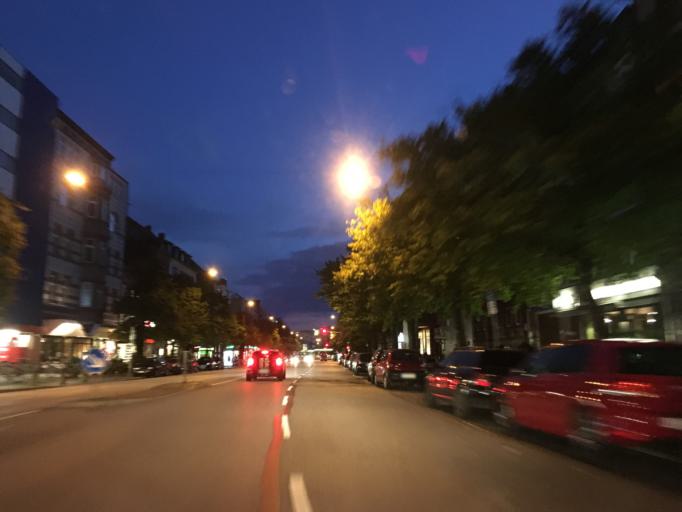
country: DE
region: Schleswig-Holstein
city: Kiel
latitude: 54.3340
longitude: 10.1330
